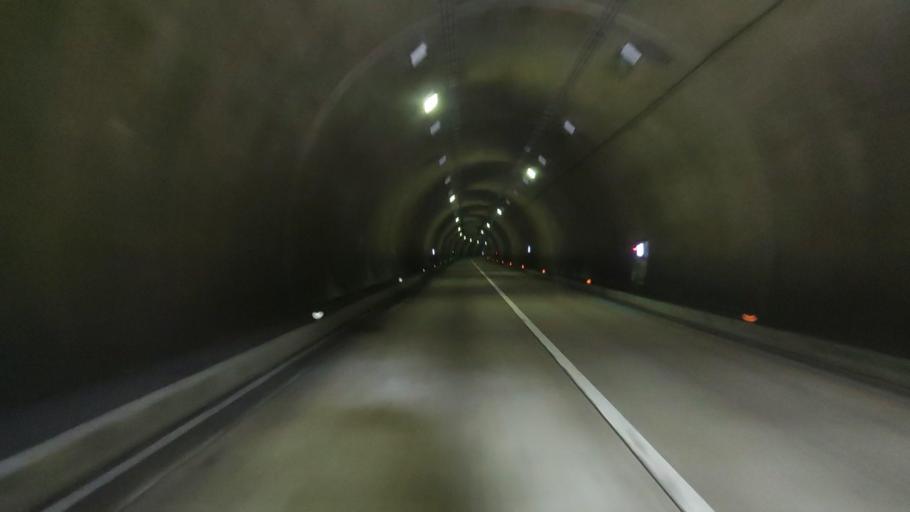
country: JP
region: Wakayama
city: Shingu
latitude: 33.8511
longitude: 135.8569
